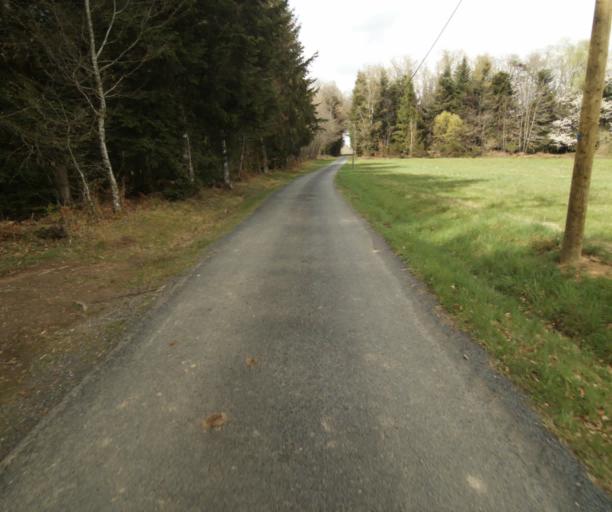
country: FR
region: Limousin
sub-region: Departement de la Correze
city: Argentat
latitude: 45.1990
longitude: 1.8952
